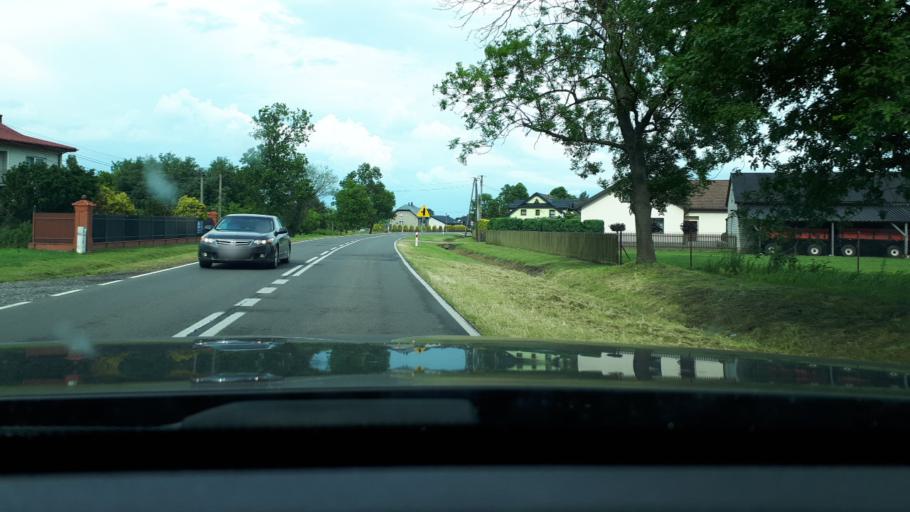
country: PL
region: Masovian Voivodeship
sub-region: Powiat sochaczewski
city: Paprotnia
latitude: 52.2640
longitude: 20.3661
